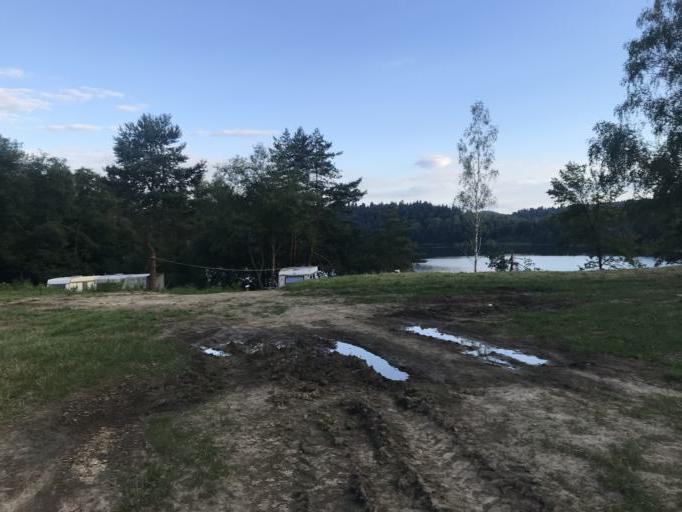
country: PL
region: Subcarpathian Voivodeship
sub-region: Powiat leski
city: Polanczyk
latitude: 49.3592
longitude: 22.4384
